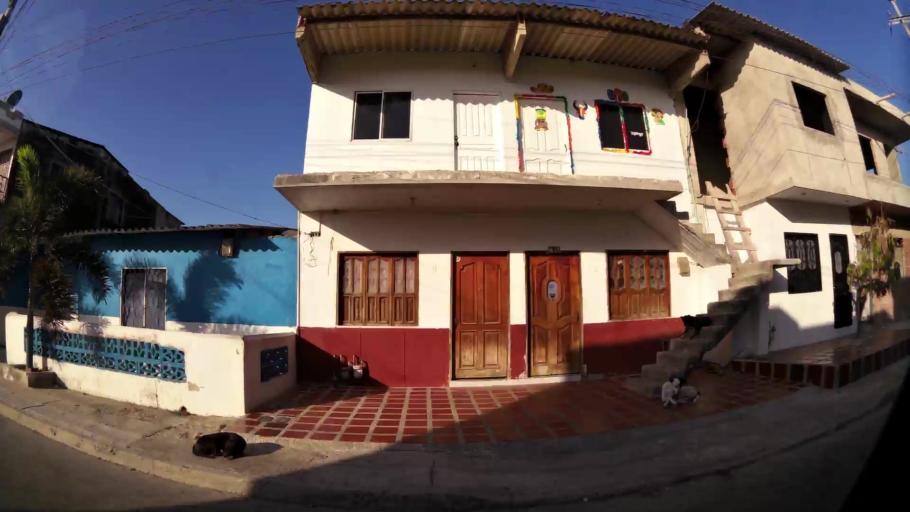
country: CO
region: Atlantico
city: Barranquilla
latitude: 11.0408
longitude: -74.8247
